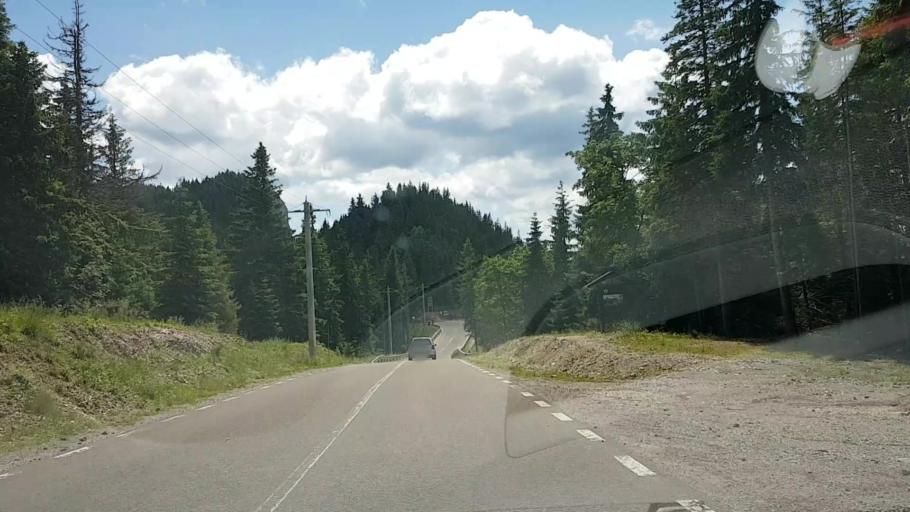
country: RO
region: Suceava
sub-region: Municipiul Campulung Moldovenesc
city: Campulung Moldovenesc
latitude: 47.4525
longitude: 25.5500
